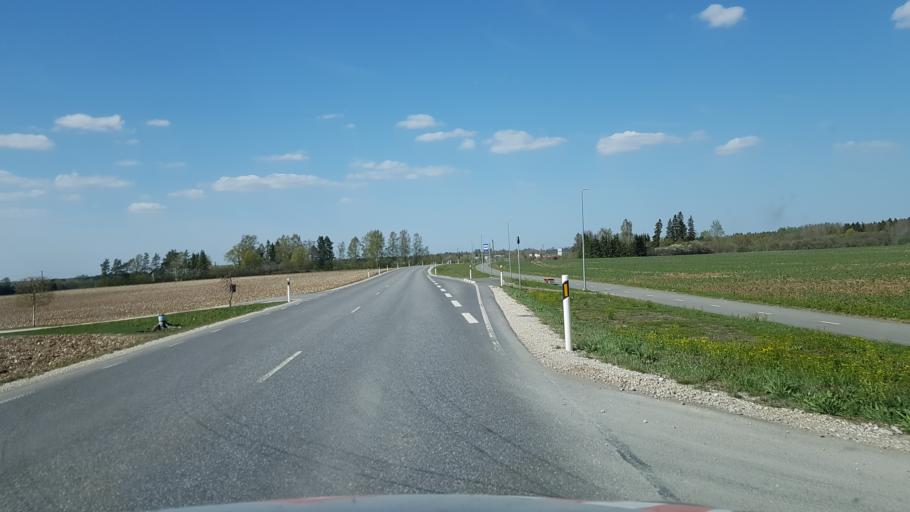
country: EE
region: Harju
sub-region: Raasiku vald
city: Arukula
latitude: 59.1907
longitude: 25.1125
